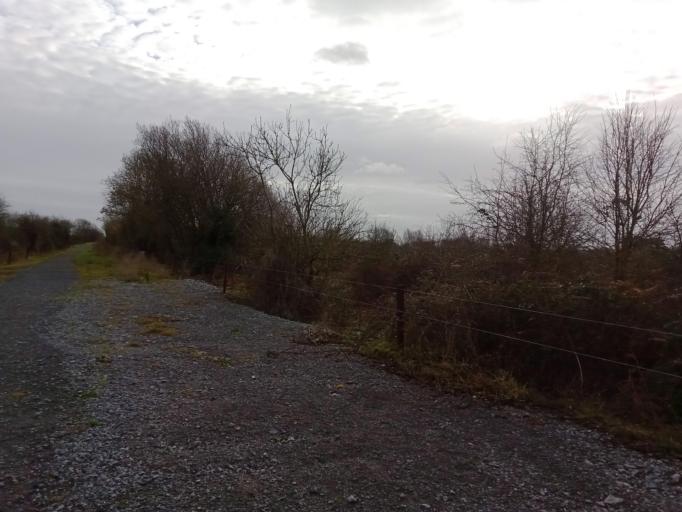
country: IE
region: Munster
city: Thurles
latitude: 52.6041
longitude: -7.7567
